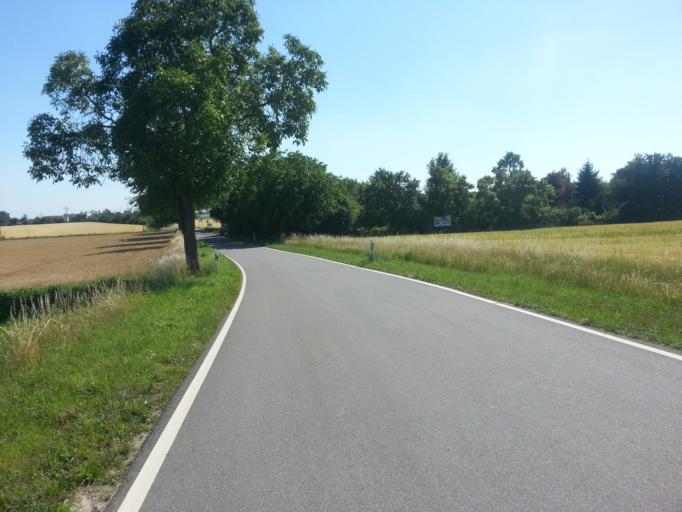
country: DE
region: Hesse
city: Viernheim
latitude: 49.5218
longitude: 8.5800
